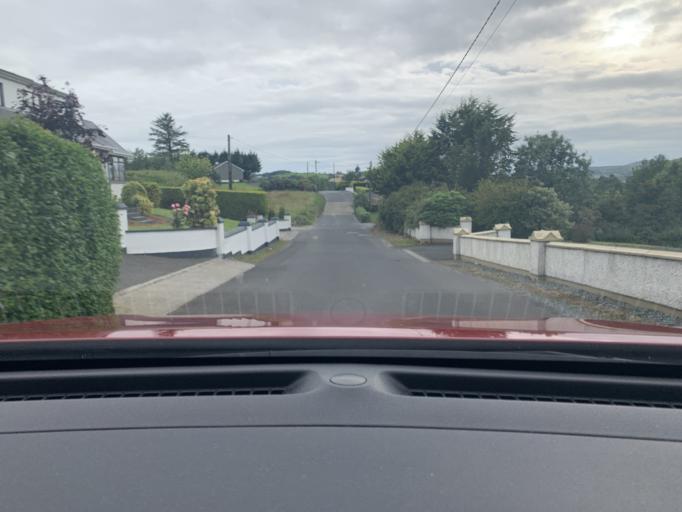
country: IE
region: Ulster
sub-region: County Donegal
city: Letterkenny
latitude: 54.9429
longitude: -7.6879
